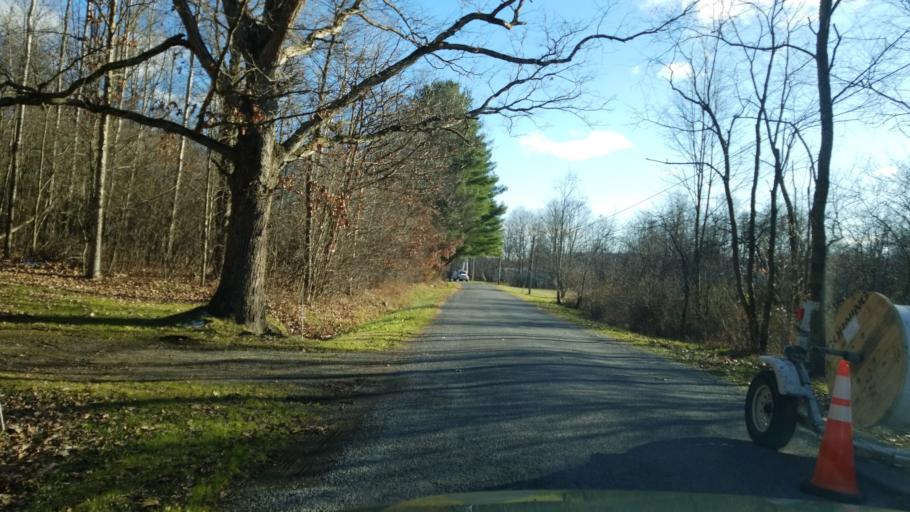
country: US
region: Pennsylvania
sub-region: Jefferson County
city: Brockway
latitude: 41.2634
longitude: -78.8039
